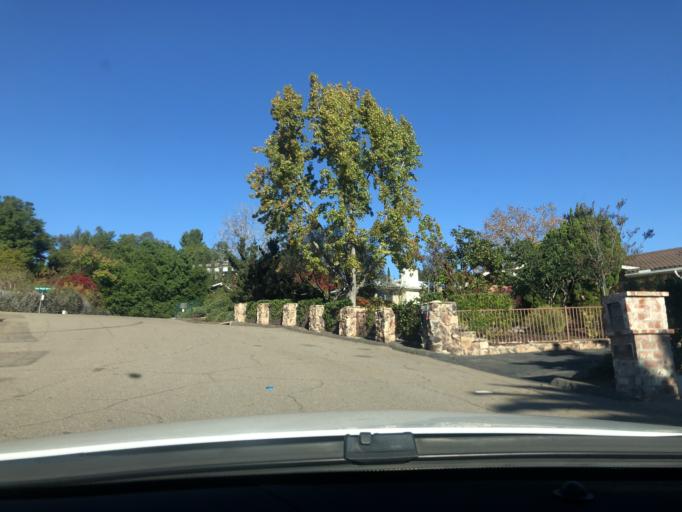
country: US
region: California
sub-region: San Diego County
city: Casa de Oro-Mount Helix
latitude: 32.7690
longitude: -116.9487
